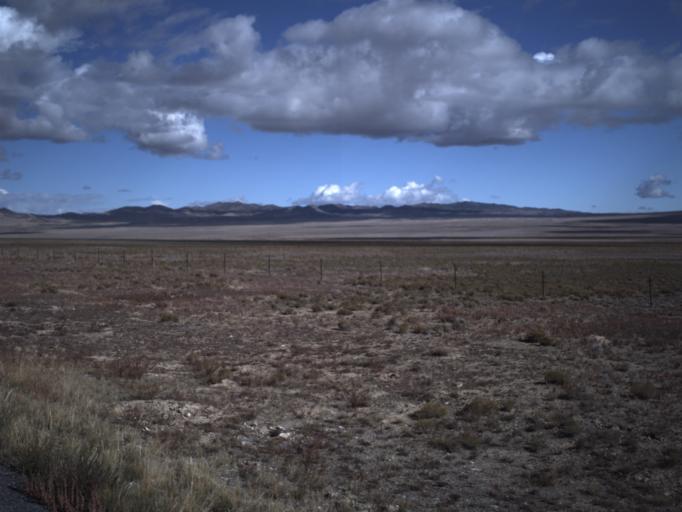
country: US
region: Utah
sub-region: Beaver County
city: Milford
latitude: 38.6494
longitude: -113.8682
